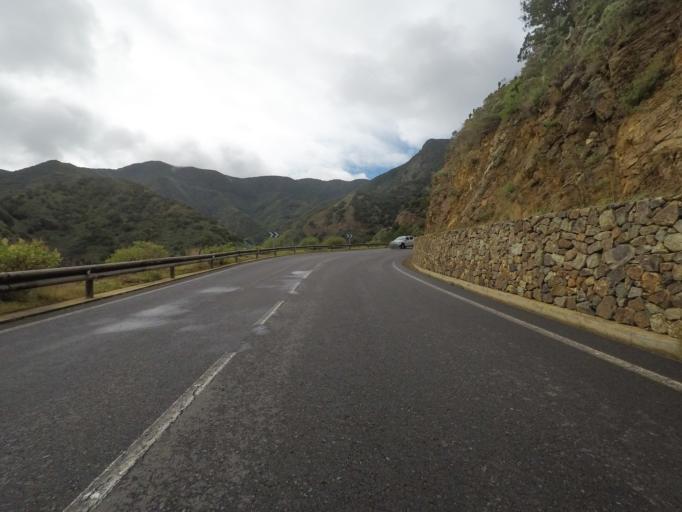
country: ES
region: Canary Islands
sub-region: Provincia de Santa Cruz de Tenerife
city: Vallehermosa
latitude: 28.1650
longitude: -17.2803
